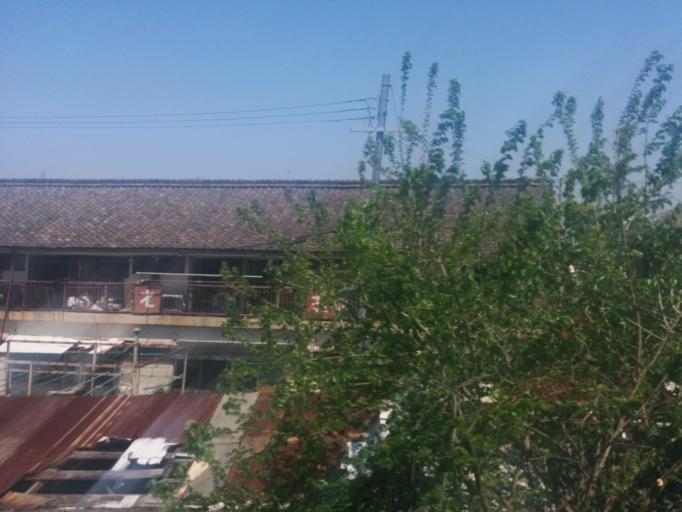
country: JP
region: Nara
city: Kashihara-shi
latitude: 34.5200
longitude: 135.7562
